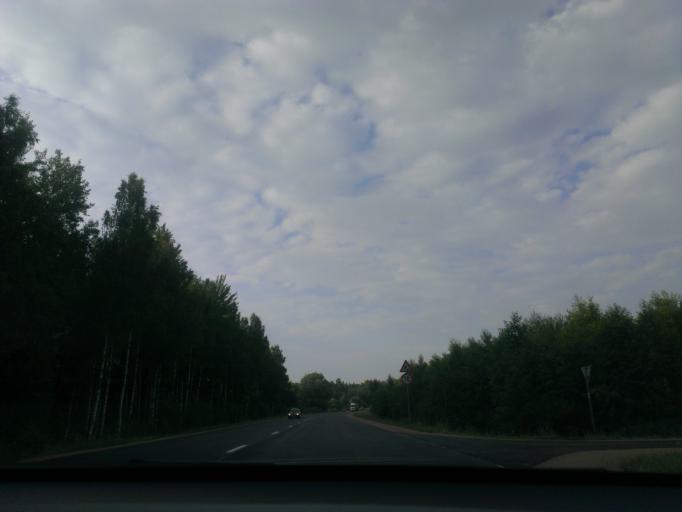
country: LV
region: Kekava
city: Kekava
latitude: 56.7135
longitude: 24.2479
